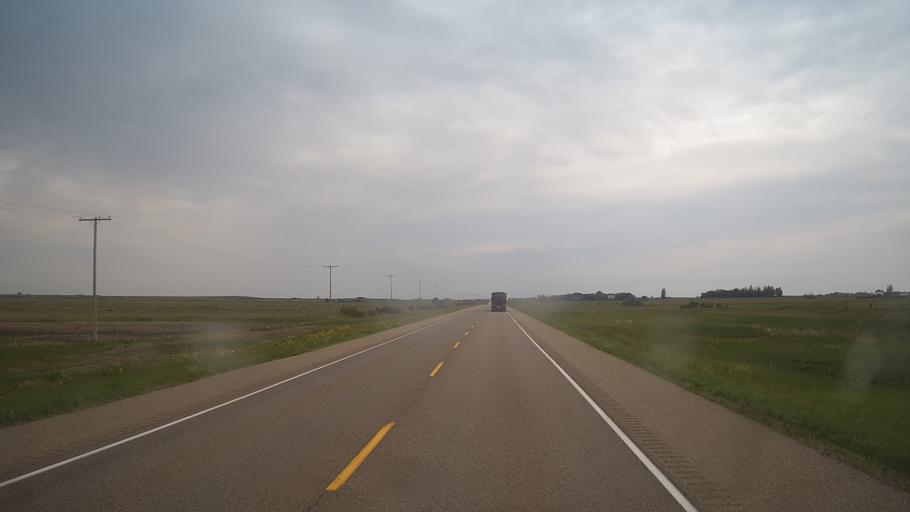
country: CA
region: Saskatchewan
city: Langham
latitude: 52.1289
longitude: -107.1528
